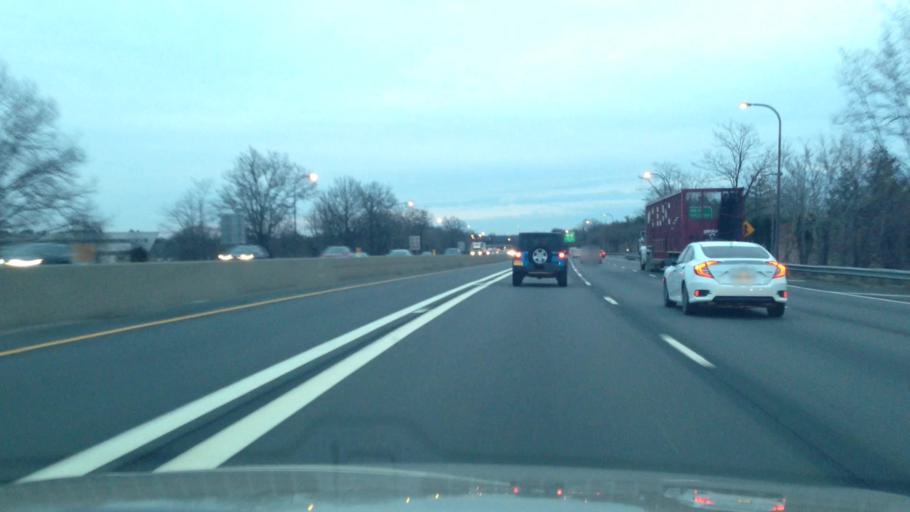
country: US
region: New York
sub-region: Nassau County
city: Jericho
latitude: 40.7831
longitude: -73.5524
